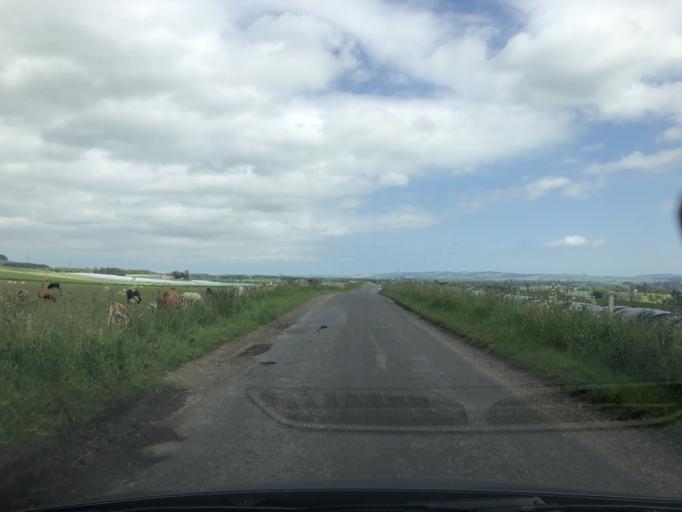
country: GB
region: Scotland
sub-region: Angus
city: Kirriemuir
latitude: 56.7232
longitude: -2.9647
